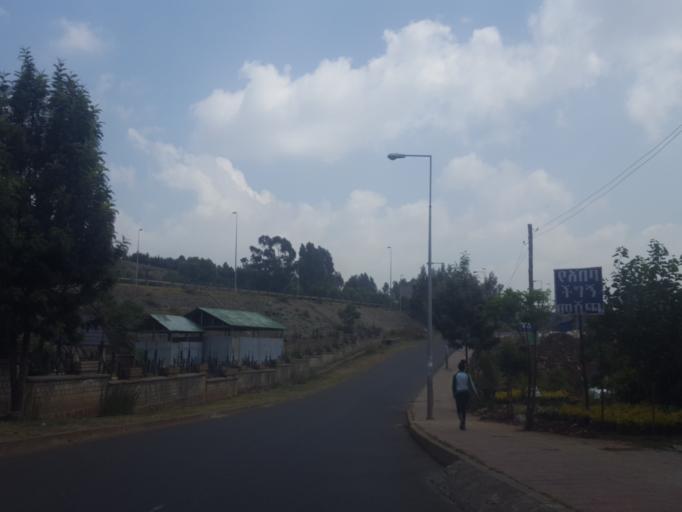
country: ET
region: Adis Abeba
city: Addis Ababa
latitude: 9.0682
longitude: 38.7230
